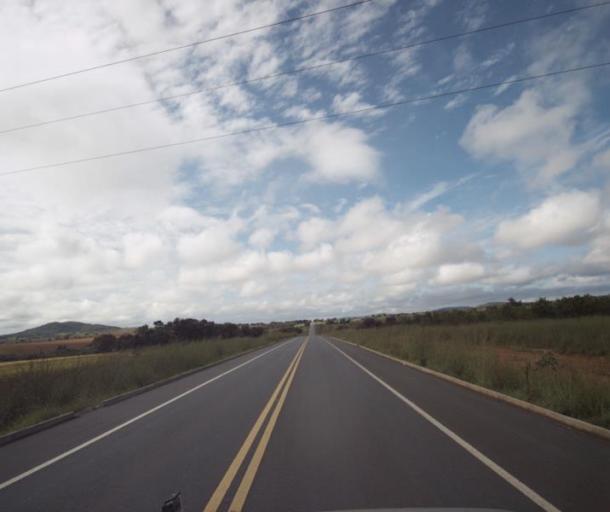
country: BR
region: Goias
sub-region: Barro Alto
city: Barro Alto
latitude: -15.2289
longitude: -48.6944
